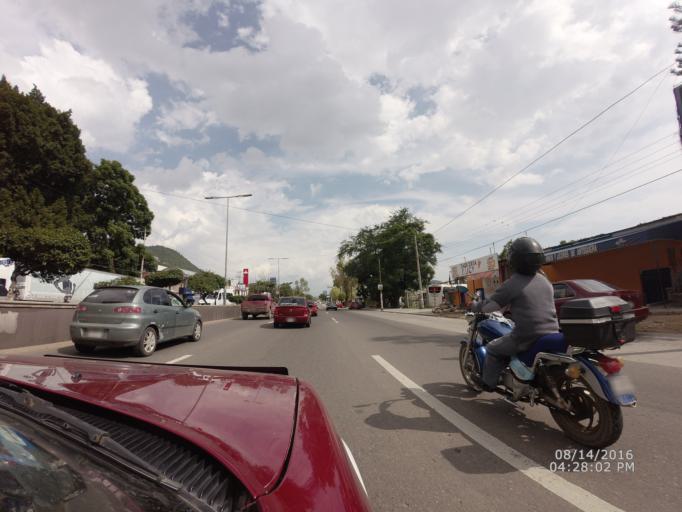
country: MX
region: Oaxaca
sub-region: Santa Maria Atzompa
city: San Jeronimo Yahuiche
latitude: 17.0900
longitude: -96.7469
